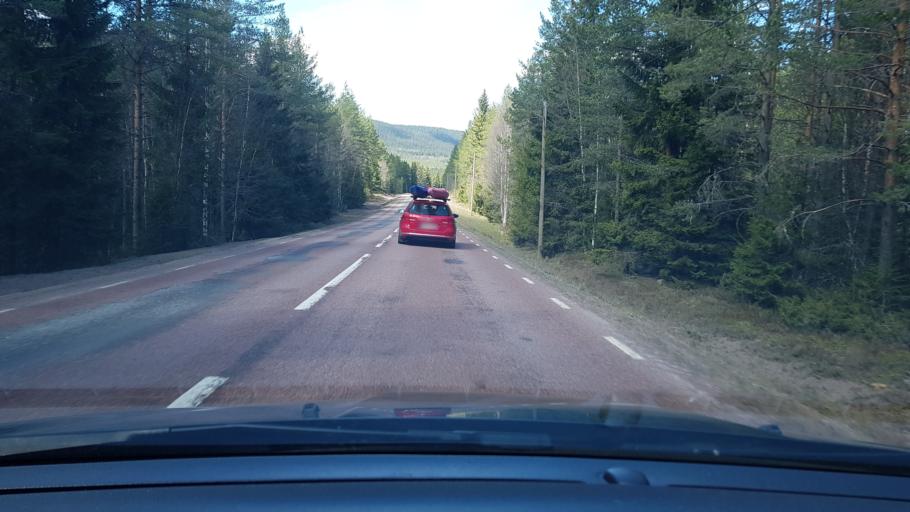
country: SE
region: Dalarna
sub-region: Malung-Saelens kommun
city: Malung
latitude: 61.0603
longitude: 13.3477
